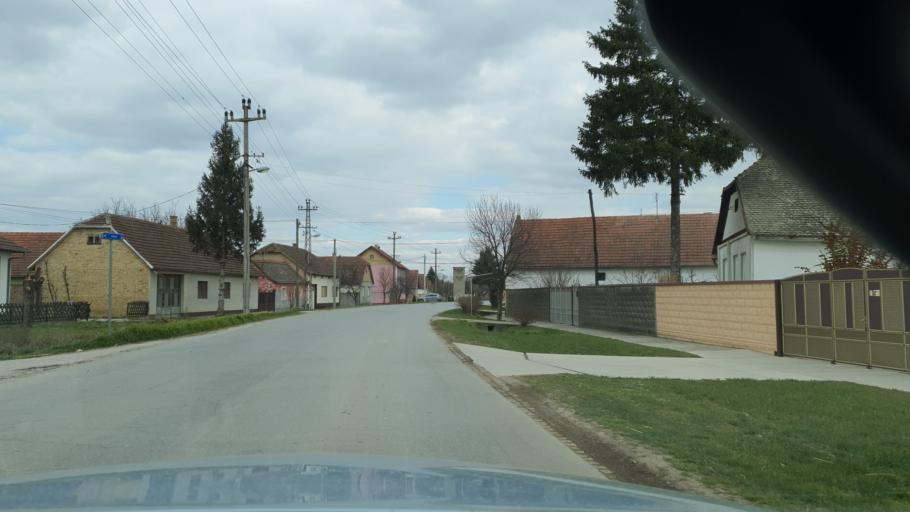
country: RS
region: Autonomna Pokrajina Vojvodina
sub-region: Juznobacki Okrug
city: Bac
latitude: 45.4062
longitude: 19.2914
